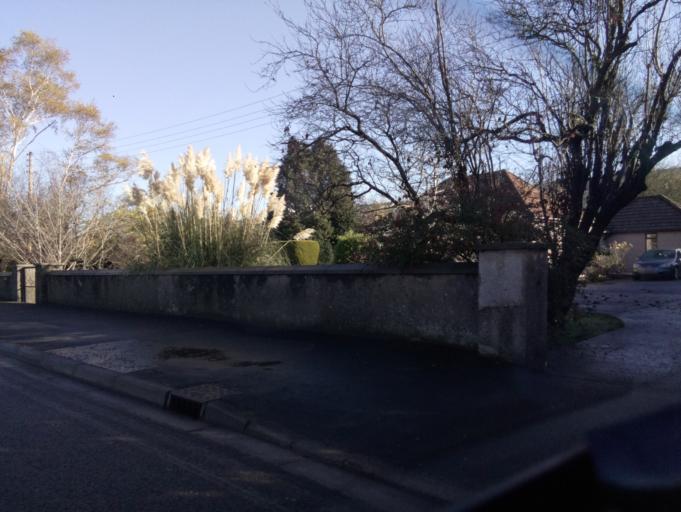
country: GB
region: England
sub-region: Somerset
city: Bridgwater
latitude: 51.1448
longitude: -2.9909
